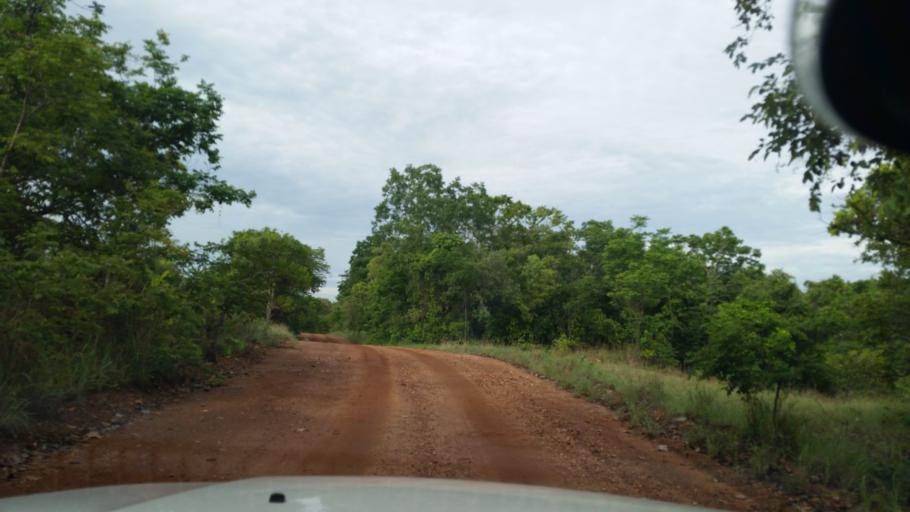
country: BR
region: Goias
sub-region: Porangatu
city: Porangatu
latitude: -13.9793
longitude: -49.2697
